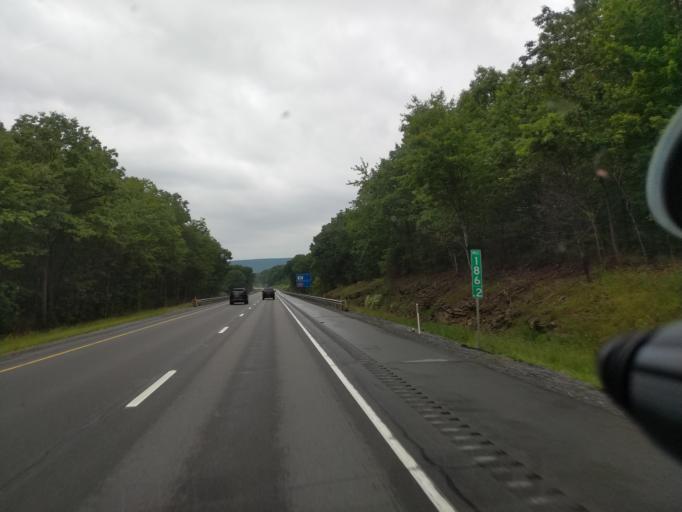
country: US
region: Pennsylvania
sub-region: Clinton County
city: Avis
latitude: 41.0532
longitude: -77.2931
